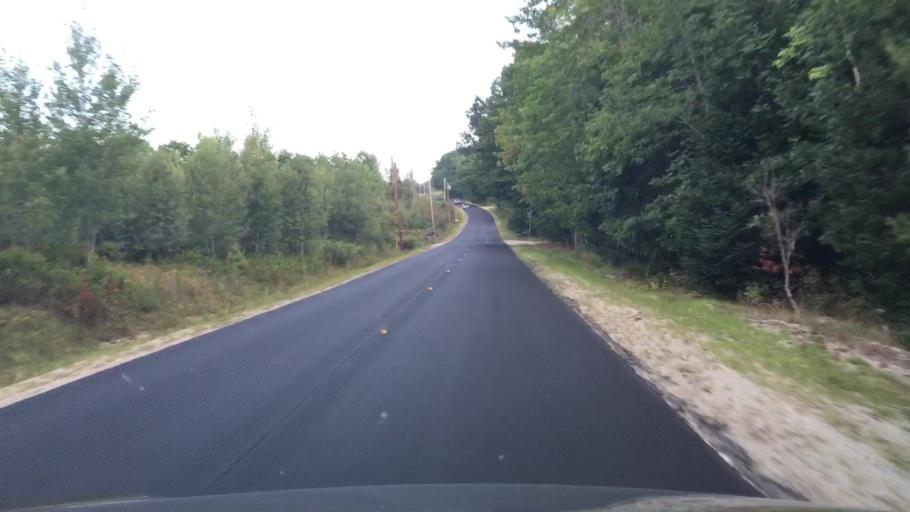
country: US
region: Maine
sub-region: Hancock County
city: Penobscot
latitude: 44.5402
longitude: -68.6160
